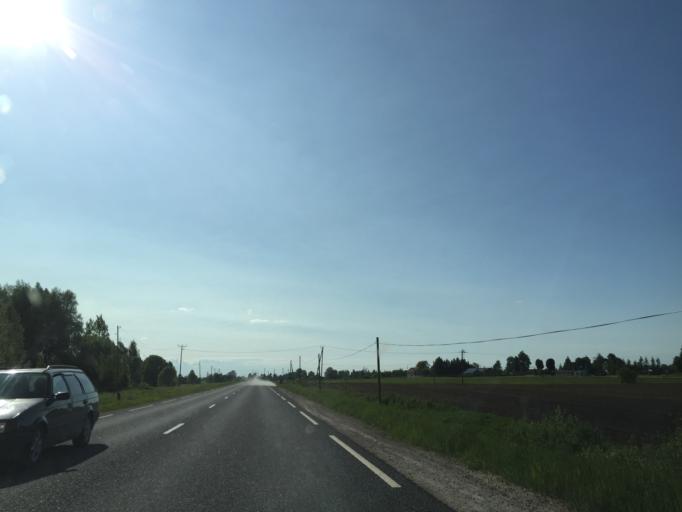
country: LV
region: Salaspils
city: Salaspils
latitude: 56.8248
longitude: 24.3745
